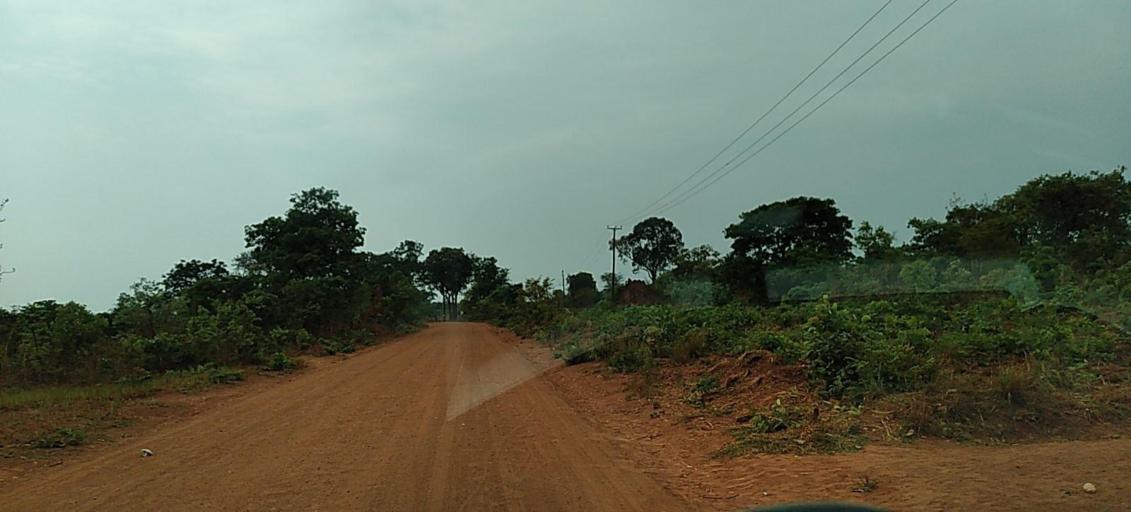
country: ZM
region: North-Western
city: Solwezi
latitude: -12.2047
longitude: 26.4961
